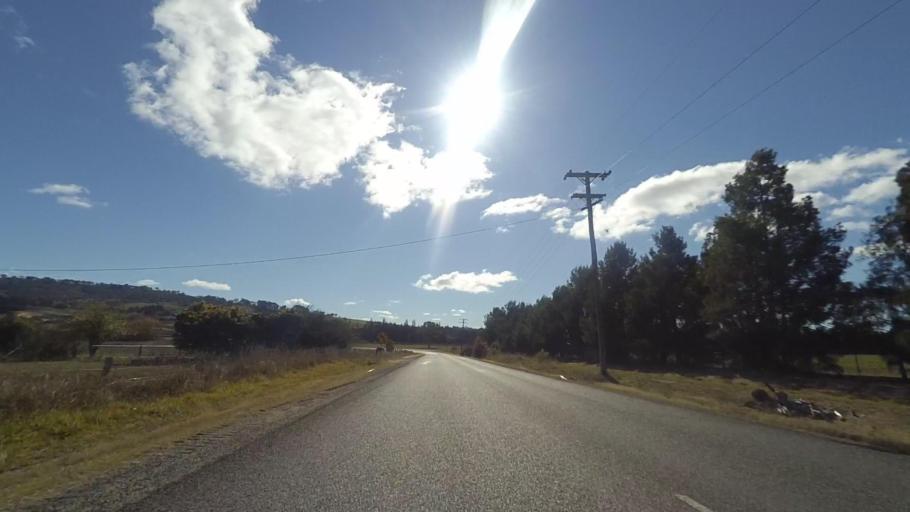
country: AU
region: New South Wales
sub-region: Bathurst Regional
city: Perthville
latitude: -33.4685
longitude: 149.5740
